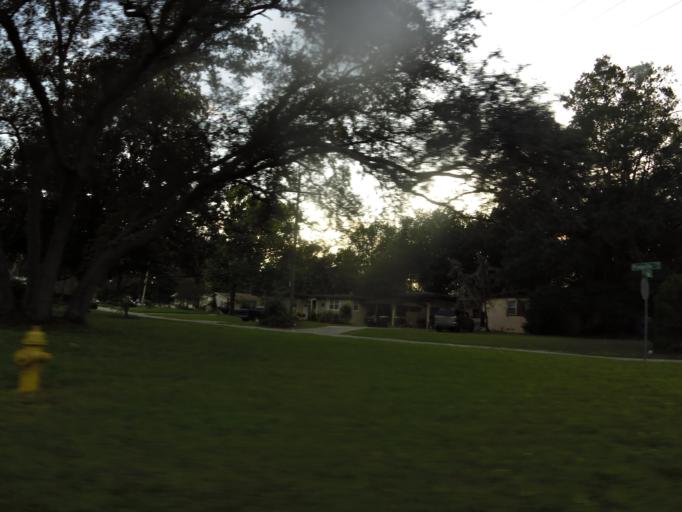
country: US
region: Florida
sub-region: Clay County
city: Orange Park
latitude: 30.2165
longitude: -81.7094
